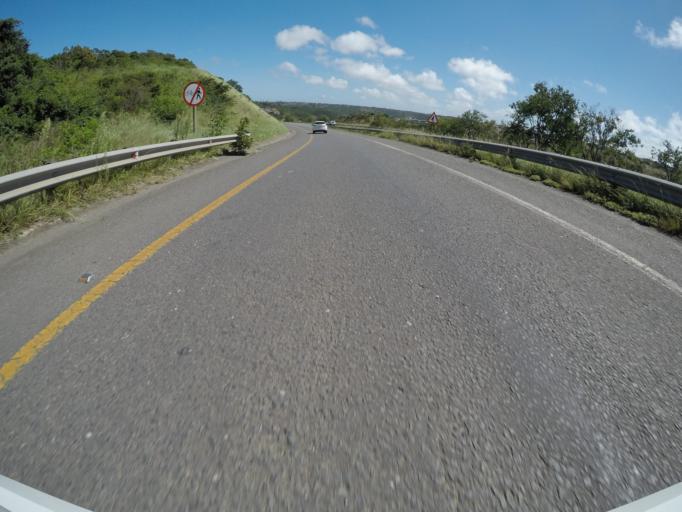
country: ZA
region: Eastern Cape
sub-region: Buffalo City Metropolitan Municipality
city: East London
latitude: -32.9541
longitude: 27.9307
